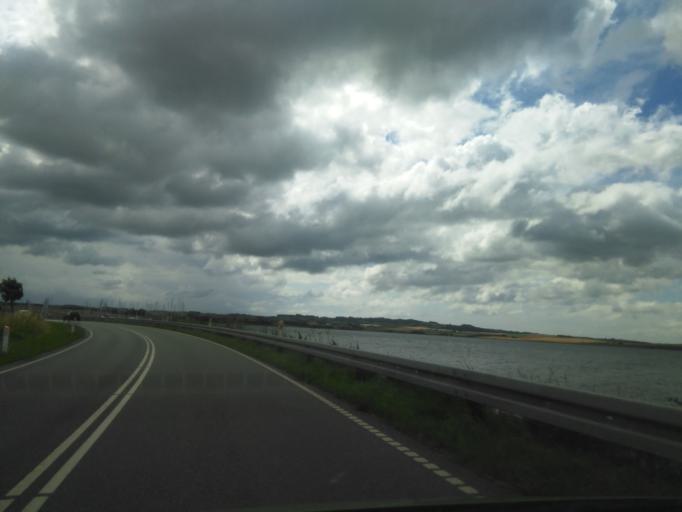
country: DK
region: Central Jutland
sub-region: Syddjurs Kommune
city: Ronde
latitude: 56.2789
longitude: 10.4892
